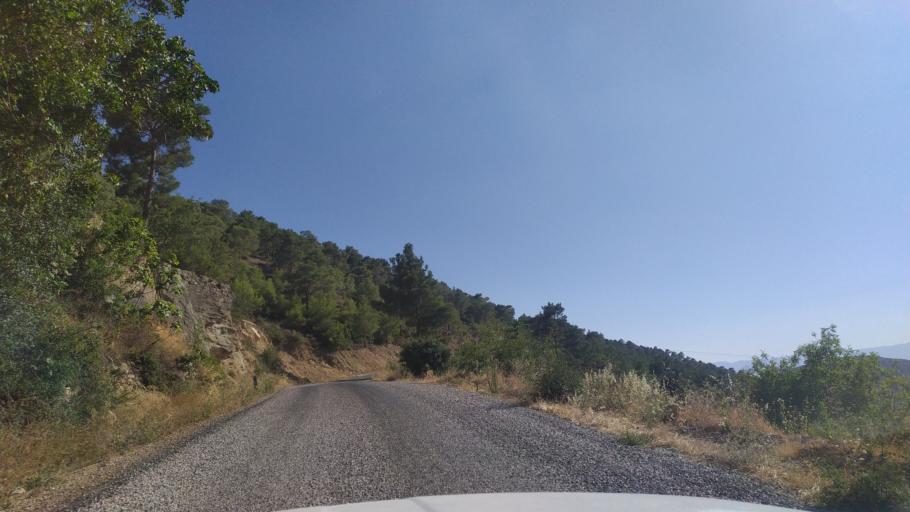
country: TR
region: Mersin
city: Mut
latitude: 36.7047
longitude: 33.4738
